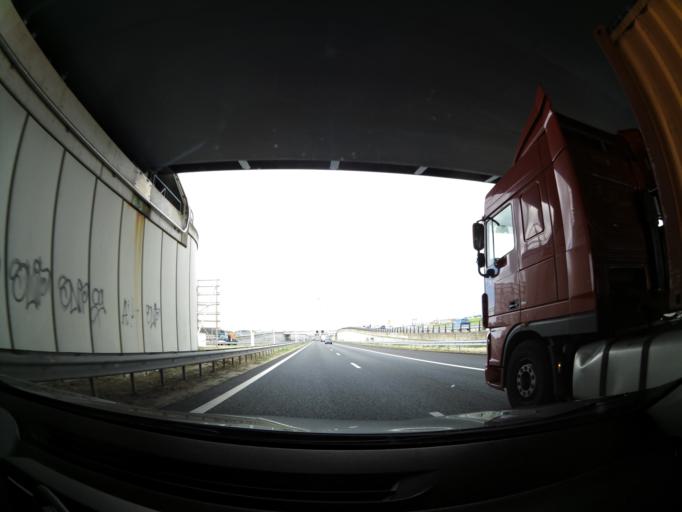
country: NL
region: South Holland
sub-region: Gemeente Maassluis
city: Maassluis
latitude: 51.9028
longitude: 4.2127
